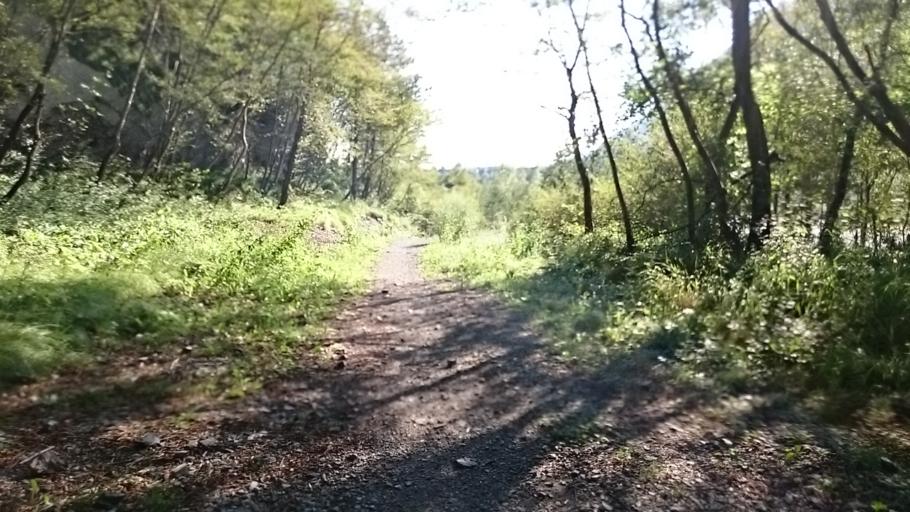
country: IT
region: Veneto
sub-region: Provincia di Belluno
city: Soverzene
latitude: 46.1959
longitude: 12.2986
